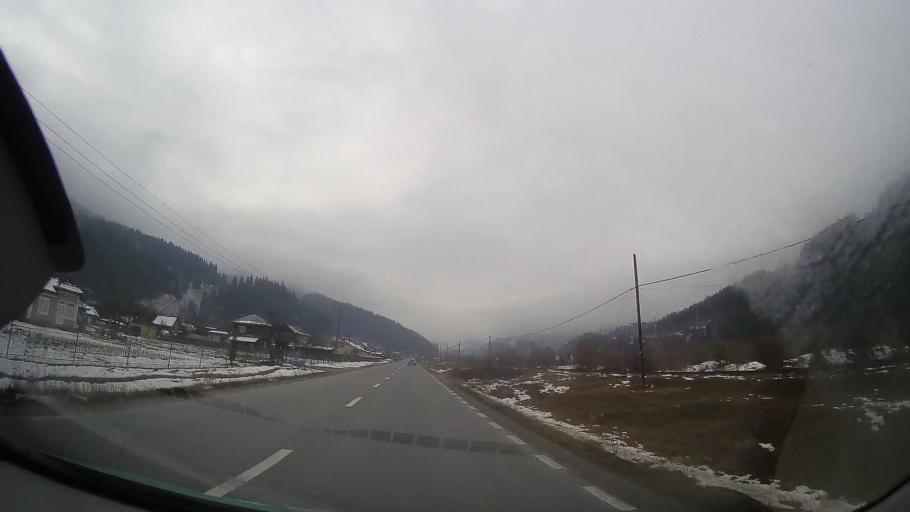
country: RO
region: Neamt
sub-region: Comuna Tasca
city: Tasca
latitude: 46.8810
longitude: 25.9924
